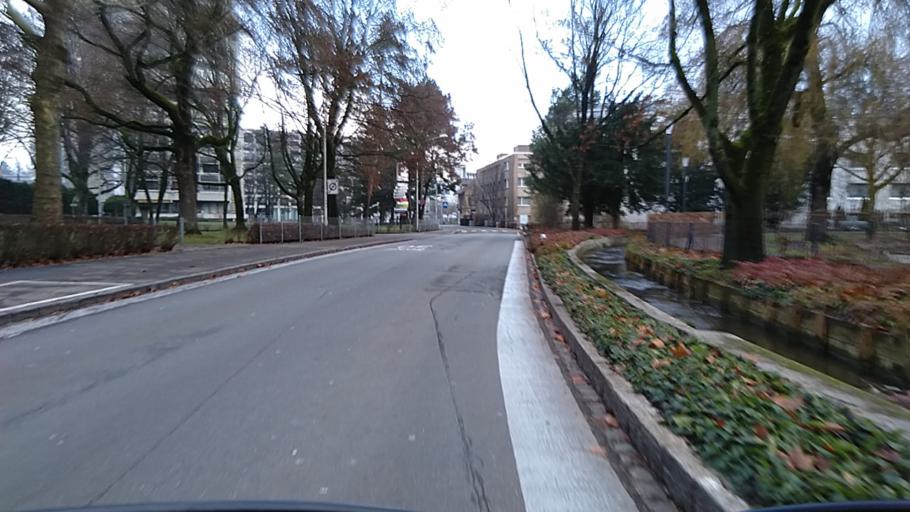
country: CH
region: Bern
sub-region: Bern-Mittelland District
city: Koniz
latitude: 46.9440
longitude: 7.3914
